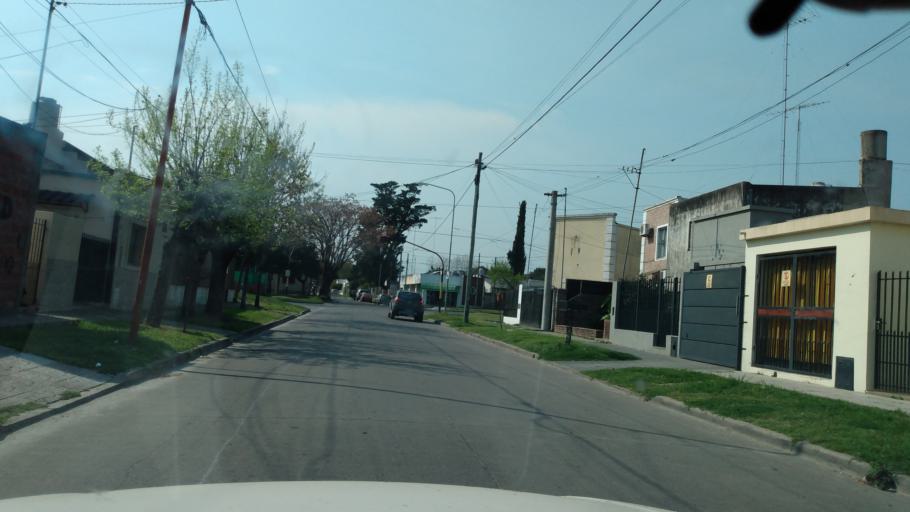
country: AR
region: Buenos Aires
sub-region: Partido de Lujan
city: Lujan
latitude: -34.5736
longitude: -59.1150
